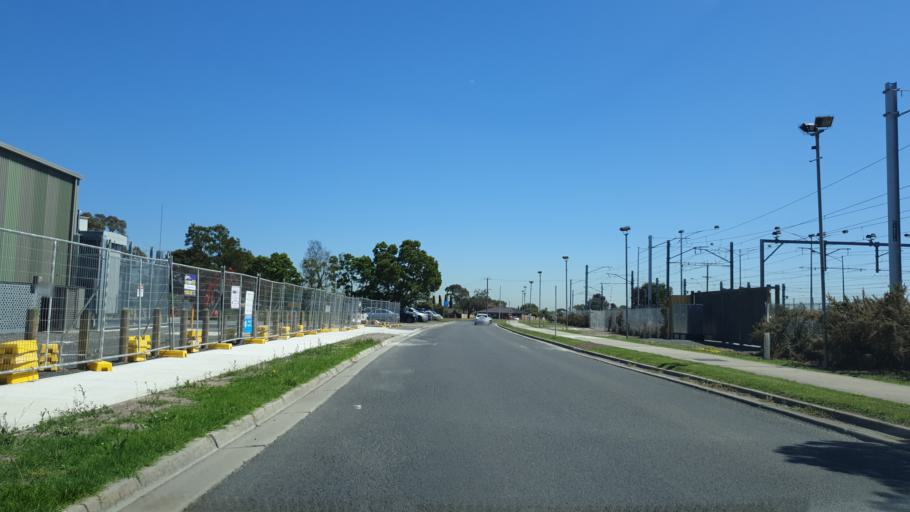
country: AU
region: Victoria
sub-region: Casey
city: Cranbourne
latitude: -38.0987
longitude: 145.2788
